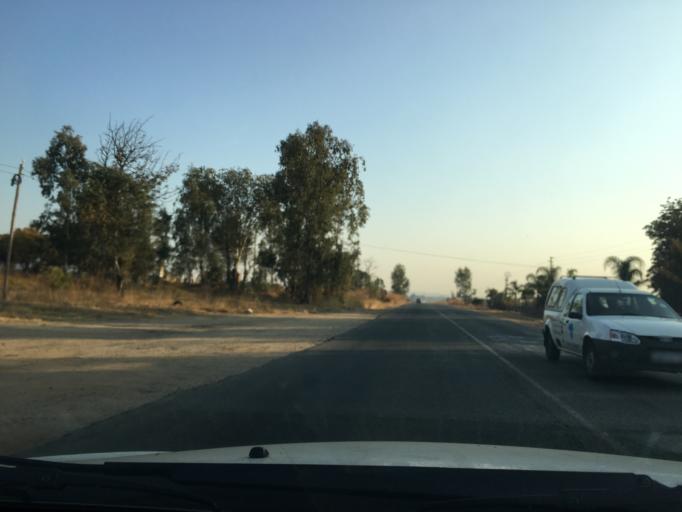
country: ZA
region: Gauteng
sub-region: West Rand District Municipality
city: Muldersdriseloop
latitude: -26.0135
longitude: 27.8588
